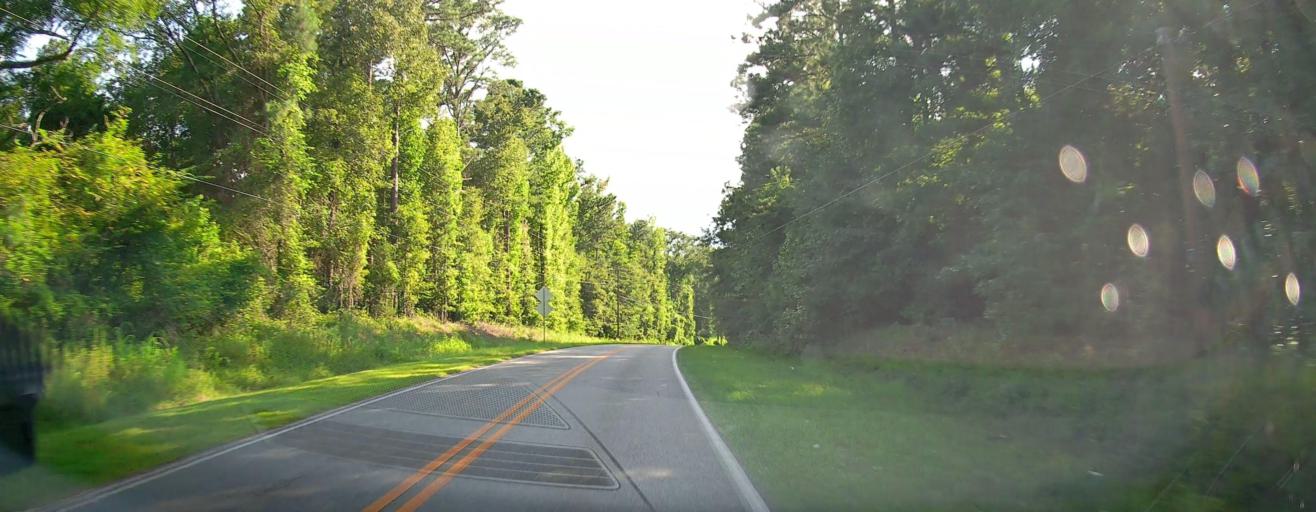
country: US
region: Georgia
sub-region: Bibb County
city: West Point
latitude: 32.7911
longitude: -83.8117
